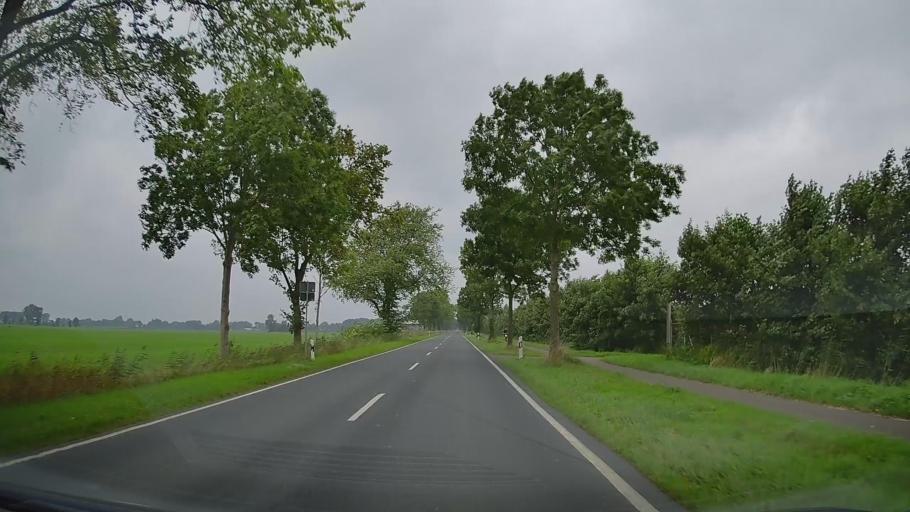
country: DE
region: Lower Saxony
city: Balje
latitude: 53.8145
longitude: 9.1307
